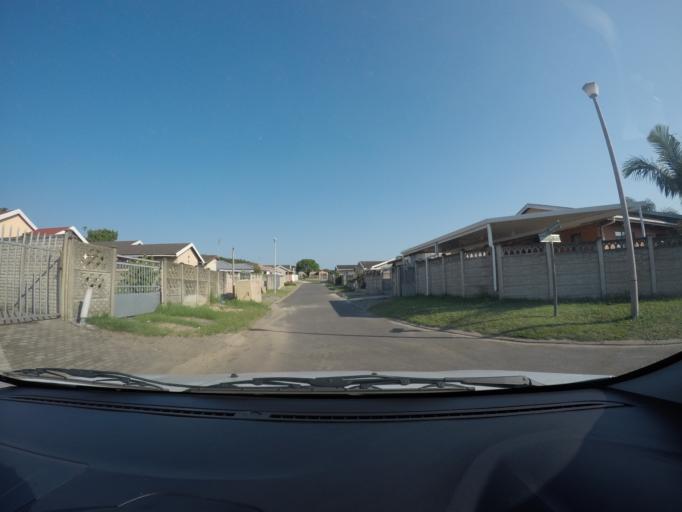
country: ZA
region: KwaZulu-Natal
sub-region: uThungulu District Municipality
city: Richards Bay
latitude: -28.7121
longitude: 32.0402
